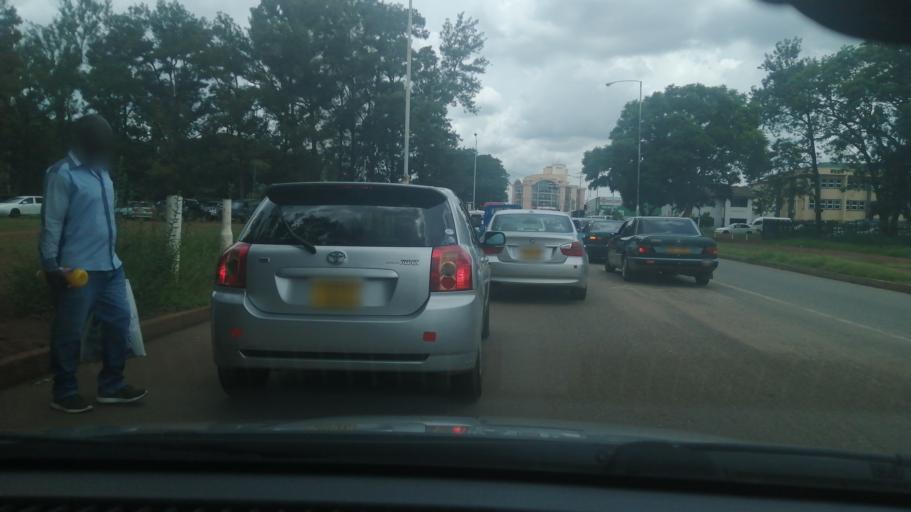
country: ZW
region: Harare
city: Harare
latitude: -17.8335
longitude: 31.0380
